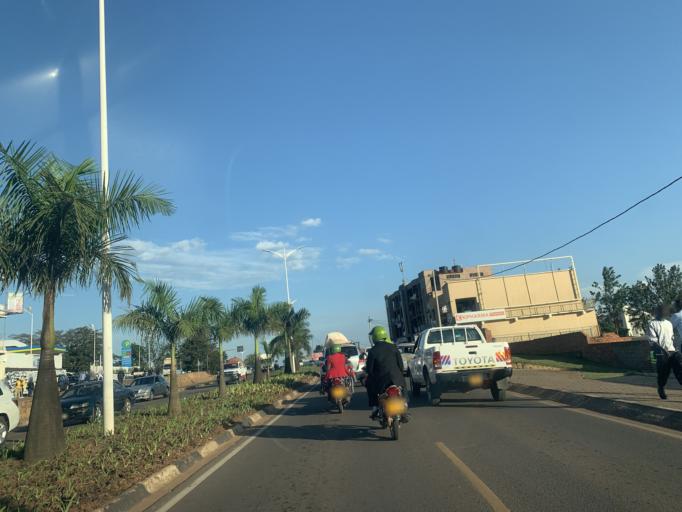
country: RW
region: Kigali
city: Kigali
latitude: -1.9604
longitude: 30.1190
